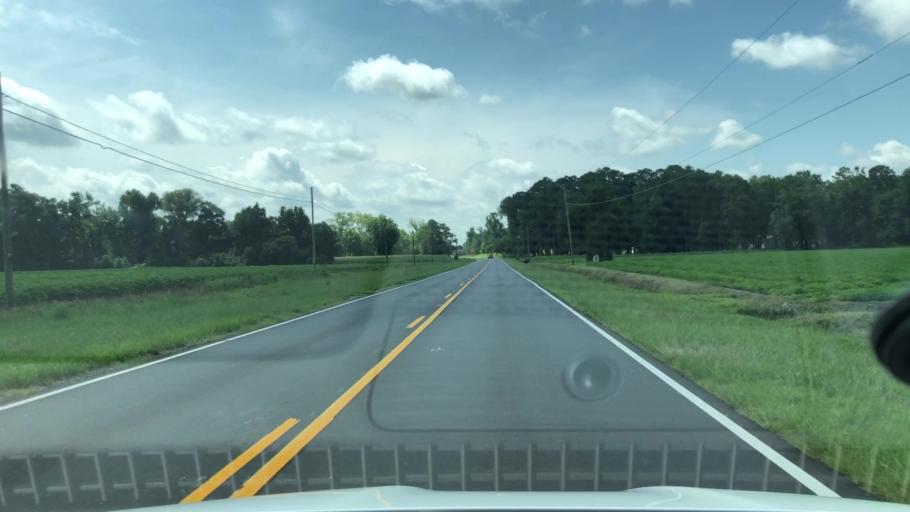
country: US
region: North Carolina
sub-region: Martin County
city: Williamston
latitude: 35.7605
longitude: -77.0750
